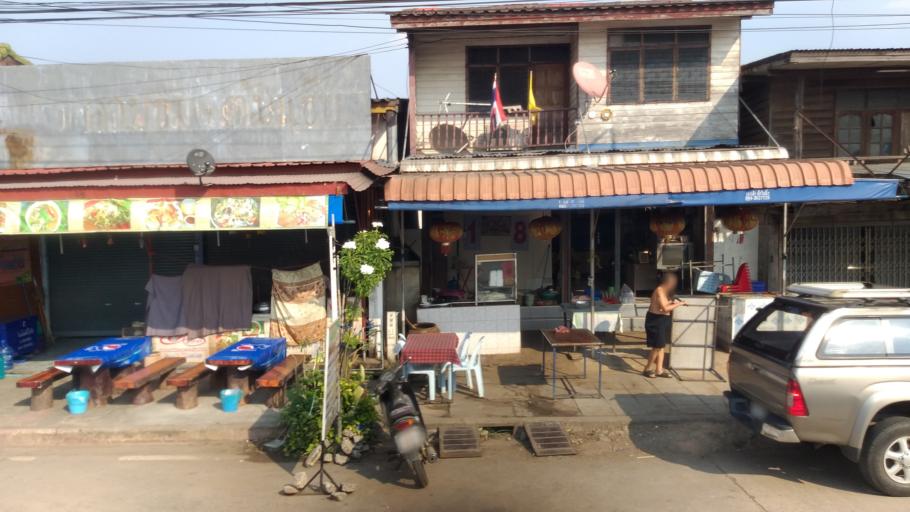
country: TH
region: Changwat Udon Thani
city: Non Sa-at
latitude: 16.9679
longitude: 102.8929
